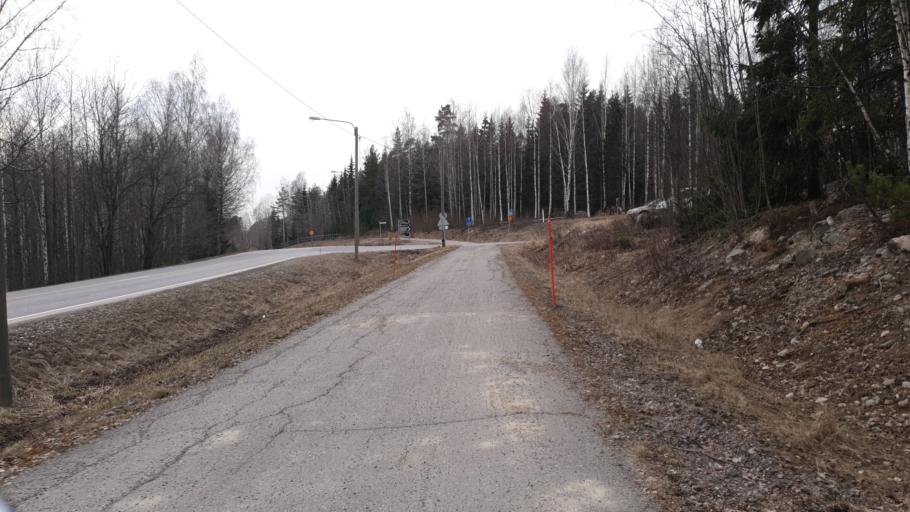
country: FI
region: Uusimaa
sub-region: Helsinki
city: Tuusula
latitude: 60.3486
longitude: 24.9106
